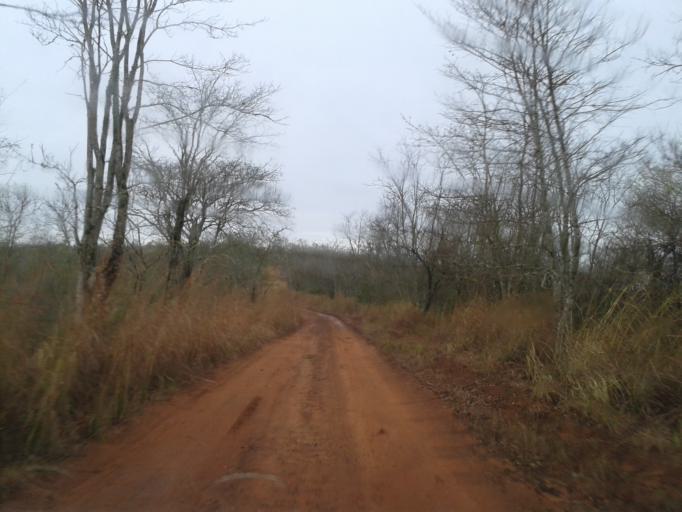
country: BR
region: Minas Gerais
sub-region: Campina Verde
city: Campina Verde
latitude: -19.3321
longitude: -49.5169
